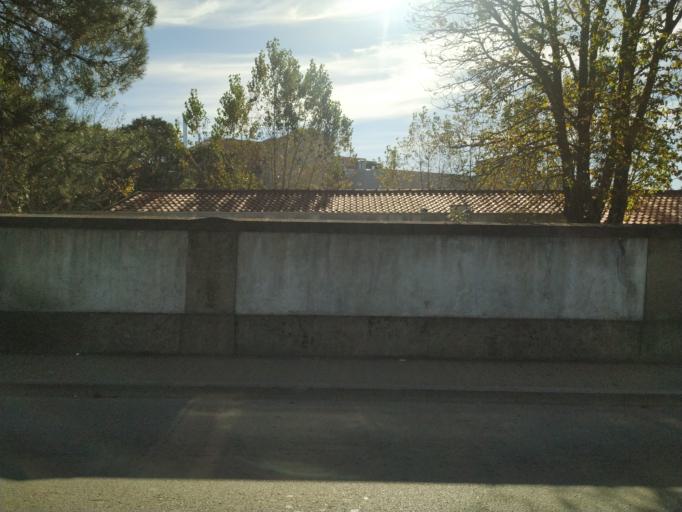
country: PT
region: Porto
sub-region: Vila Nova de Gaia
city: Vilar de Andorinho
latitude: 41.1054
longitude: -8.5908
